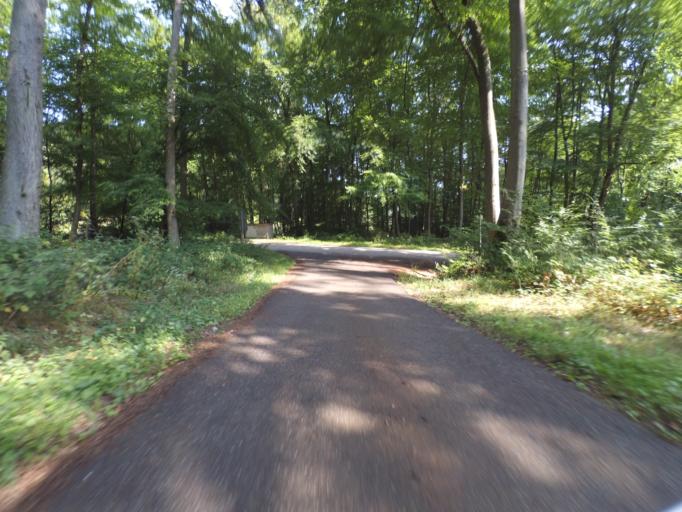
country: DE
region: Saarland
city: Orscholz
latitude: 49.4781
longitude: 6.5508
